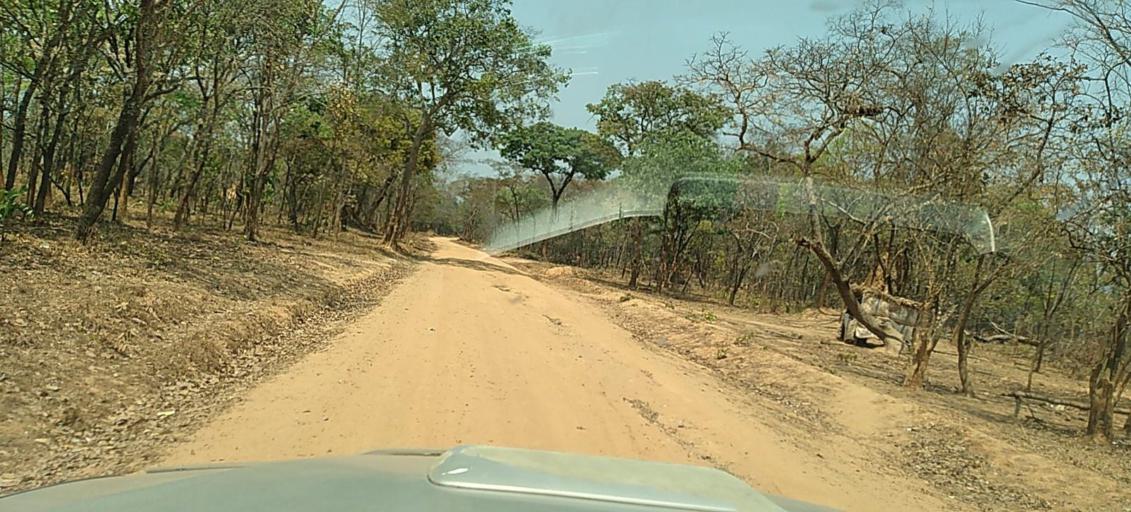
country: ZM
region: North-Western
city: Kasempa
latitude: -13.6644
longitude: 26.2801
